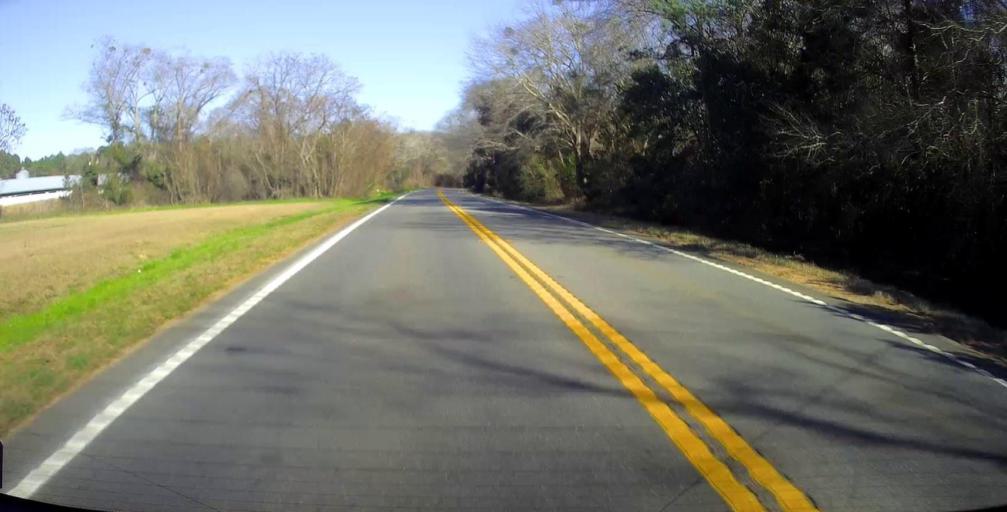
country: US
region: Georgia
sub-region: Macon County
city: Oglethorpe
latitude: 32.3516
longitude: -84.1594
